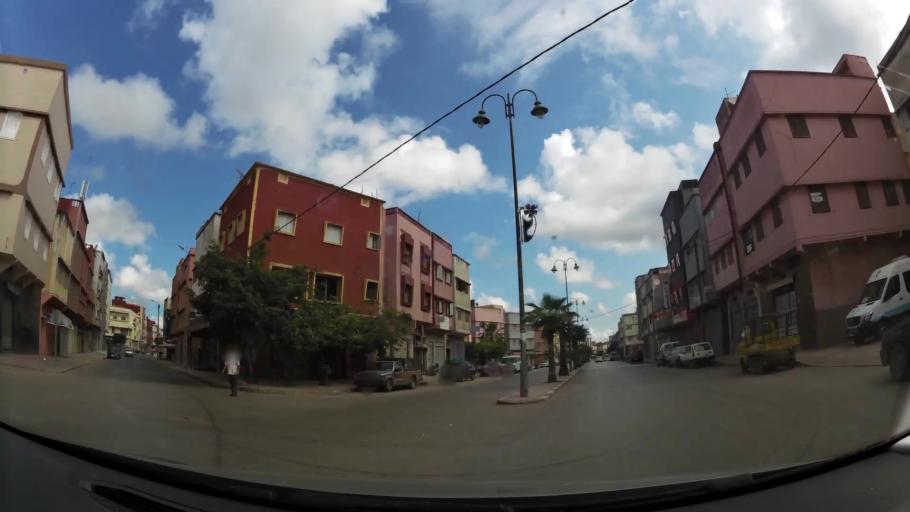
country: MA
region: Gharb-Chrarda-Beni Hssen
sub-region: Kenitra Province
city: Kenitra
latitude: 34.2667
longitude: -6.5613
